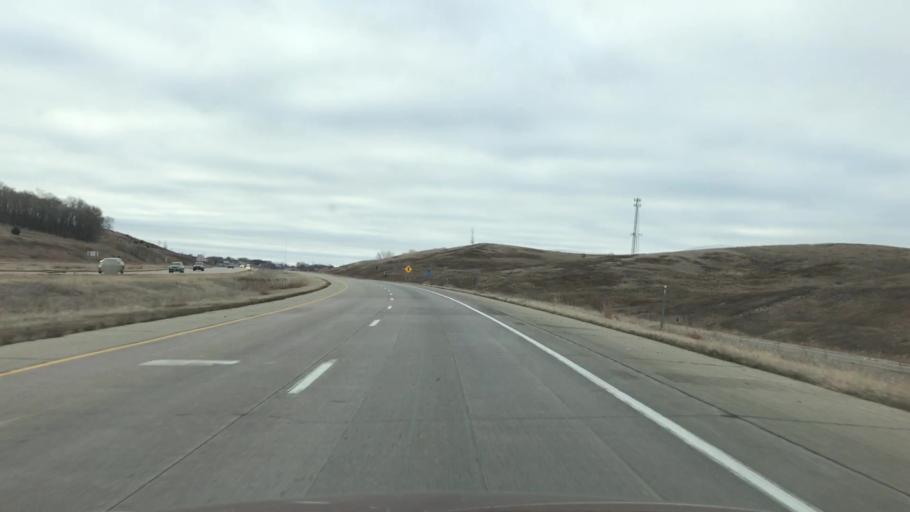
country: US
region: Iowa
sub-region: Woodbury County
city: Sioux City
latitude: 42.5177
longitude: -96.3384
